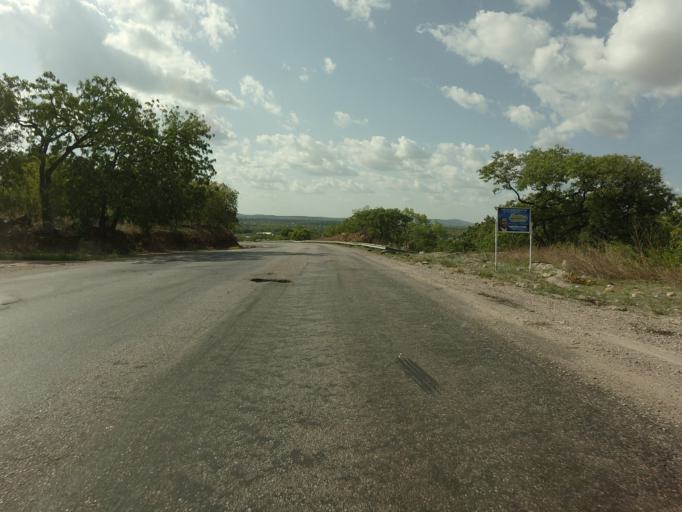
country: GH
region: Upper East
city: Bolgatanga
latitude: 10.5543
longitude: -0.8303
